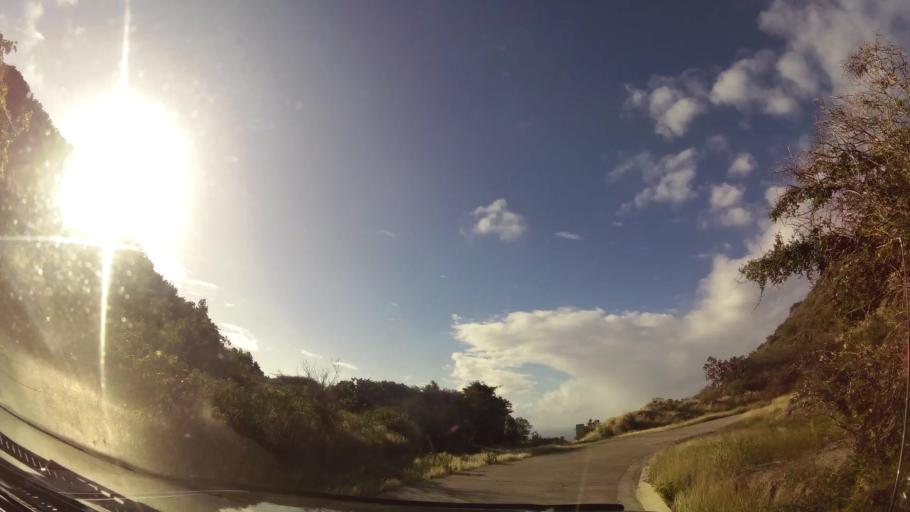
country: MS
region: Saint Peter
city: Brades
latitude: 16.8090
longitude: -62.1930
